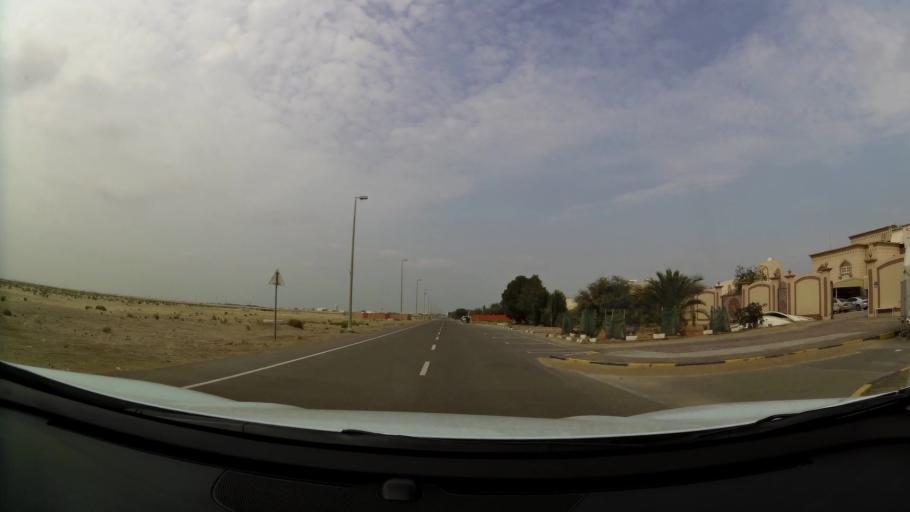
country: AE
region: Abu Dhabi
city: Abu Dhabi
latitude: 24.6328
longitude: 54.6763
